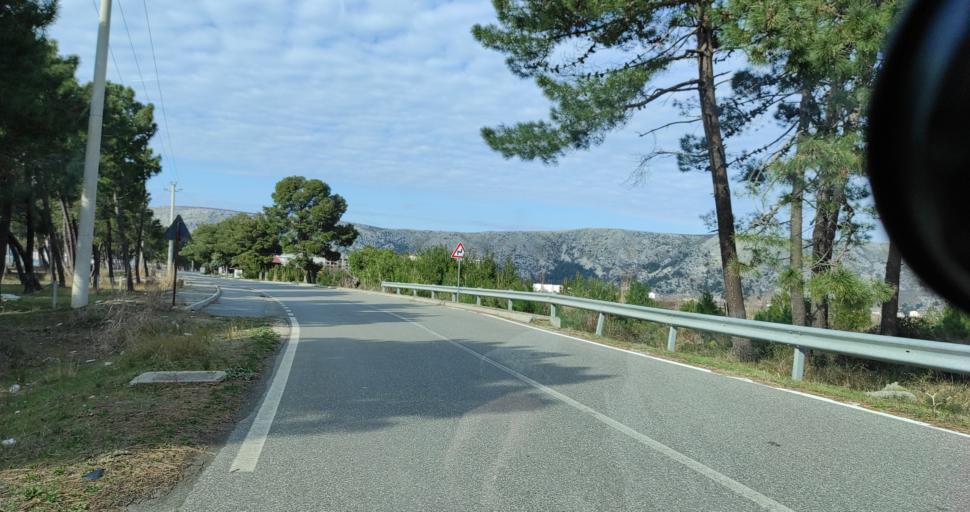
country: AL
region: Lezhe
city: Shengjin
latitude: 41.7862
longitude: 19.6036
